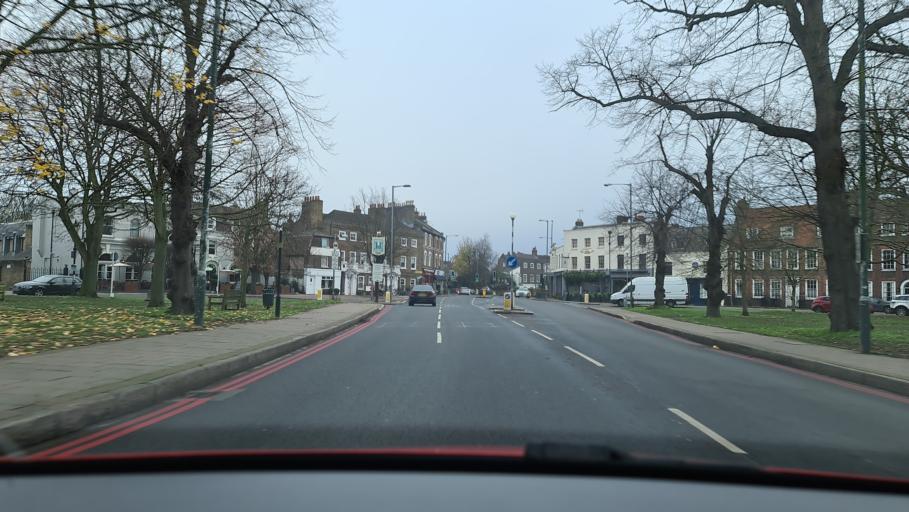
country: GB
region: England
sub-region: Greater London
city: Brentford
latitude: 51.4840
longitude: -0.2872
